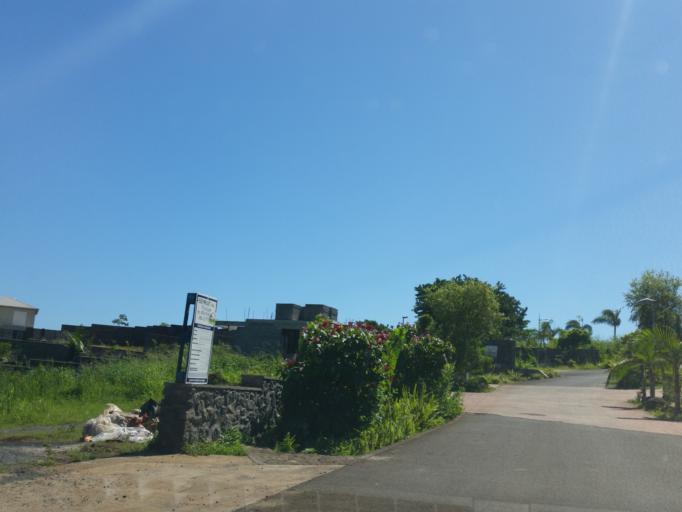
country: RE
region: Reunion
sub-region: Reunion
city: Sainte-Marie
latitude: -20.9173
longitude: 55.5235
